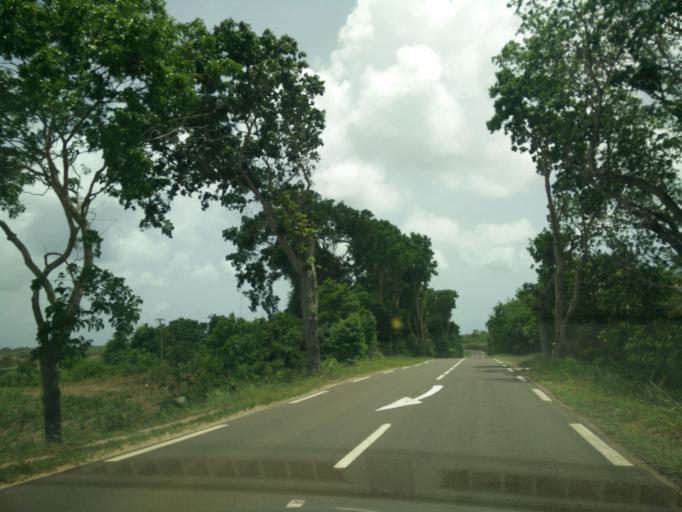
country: GP
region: Guadeloupe
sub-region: Guadeloupe
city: Port-Louis
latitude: 16.4353
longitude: -61.5123
